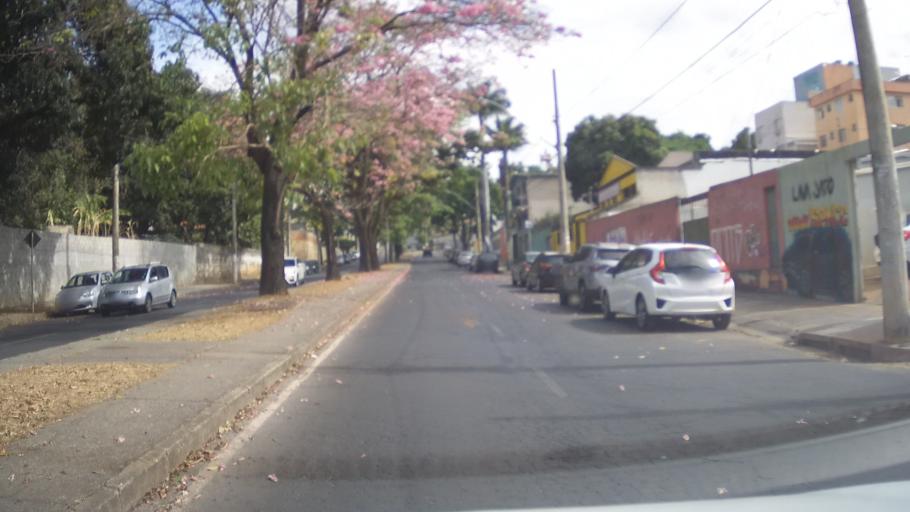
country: BR
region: Minas Gerais
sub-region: Belo Horizonte
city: Belo Horizonte
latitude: -19.8414
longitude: -43.9741
